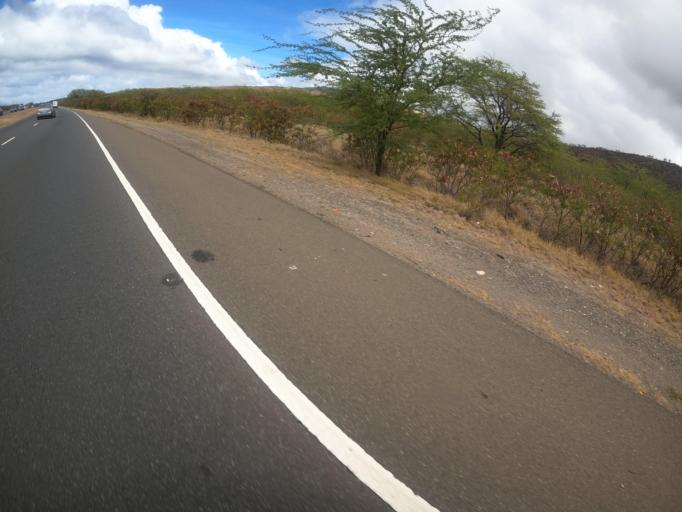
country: US
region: Hawaii
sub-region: Honolulu County
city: Makakilo City
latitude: 21.3366
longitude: -158.0961
